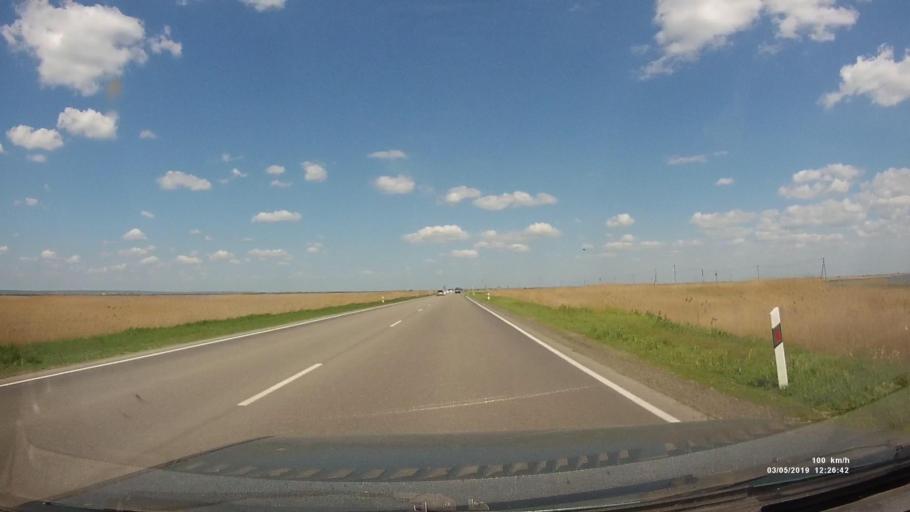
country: RU
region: Rostov
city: Semikarakorsk
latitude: 47.4496
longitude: 40.7158
